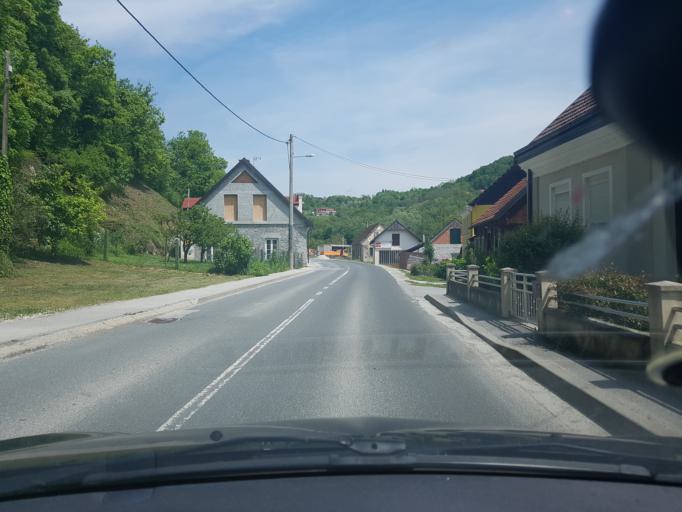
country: HR
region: Krapinsko-Zagorska
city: Pregrada
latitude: 46.1680
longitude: 15.7519
